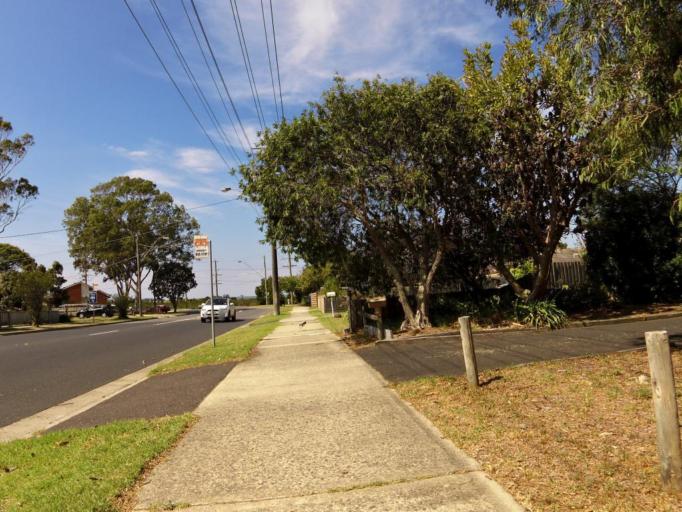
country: AU
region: Victoria
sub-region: Mornington Peninsula
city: Hastings
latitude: -38.3161
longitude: 145.1923
